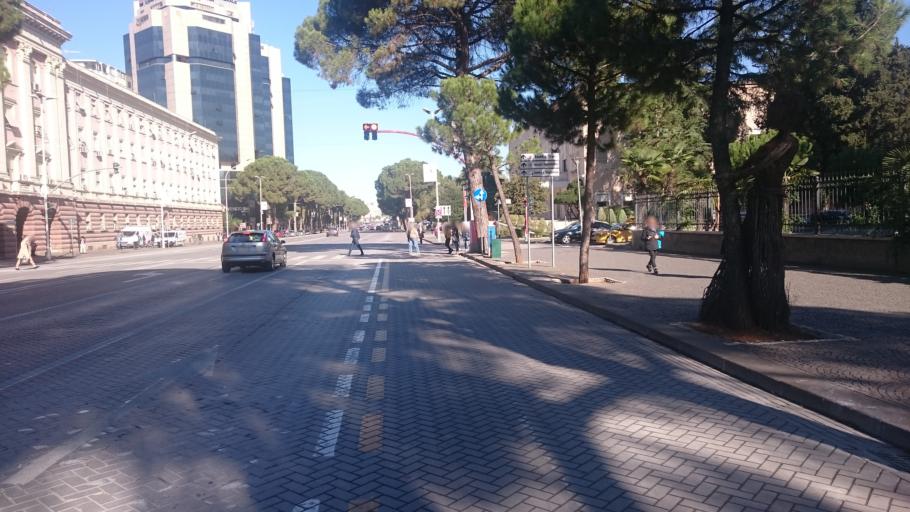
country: AL
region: Tirane
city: Tirana
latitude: 41.3208
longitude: 19.8206
